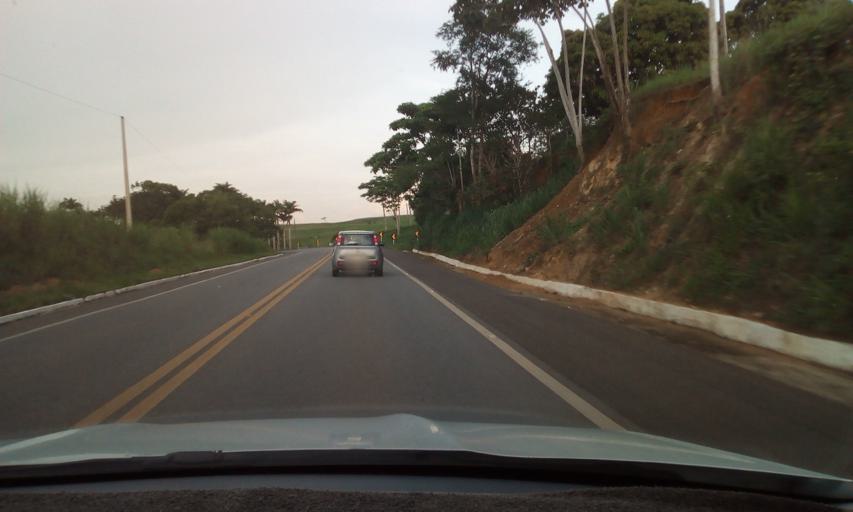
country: BR
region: Pernambuco
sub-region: Vicencia
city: Vicencia
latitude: -7.6293
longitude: -35.2487
